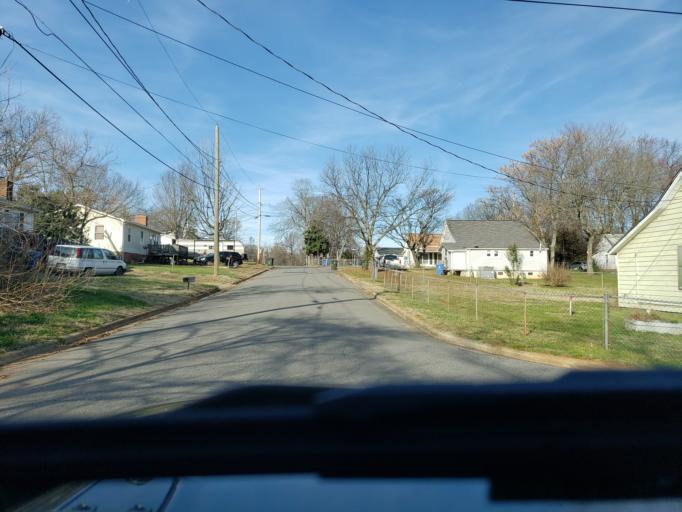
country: US
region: North Carolina
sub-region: Cleveland County
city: Kings Mountain
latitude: 35.2466
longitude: -81.3346
